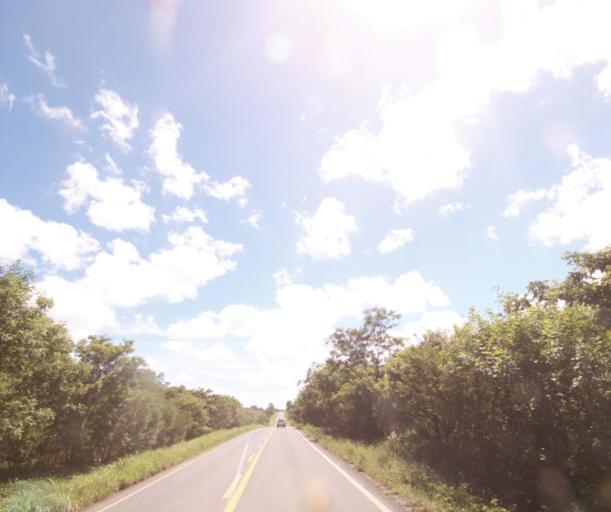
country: BR
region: Bahia
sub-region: Sao Felix Do Coribe
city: Santa Maria da Vitoria
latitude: -13.4045
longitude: -44.1534
